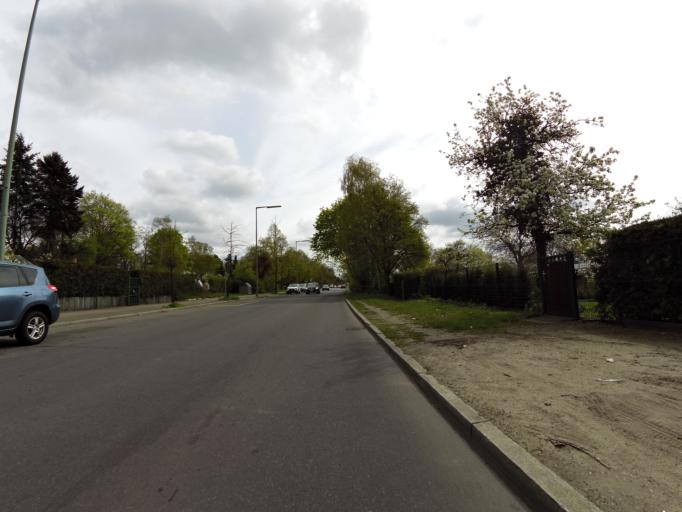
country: DE
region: Berlin
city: Tempelhof Bezirk
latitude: 52.4527
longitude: 13.4056
